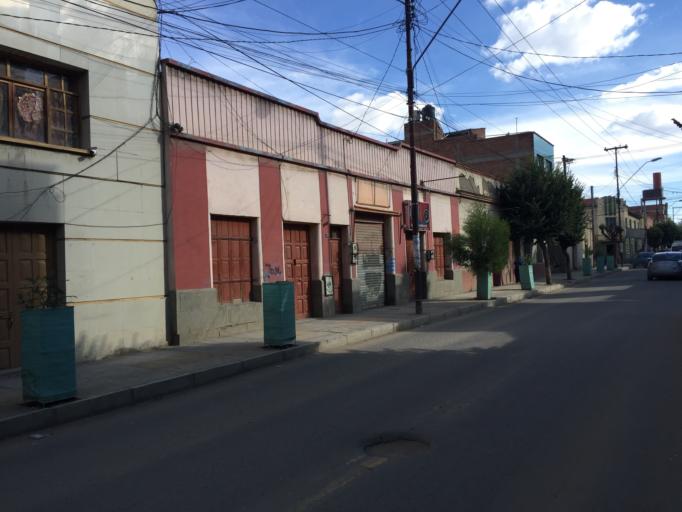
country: BO
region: Oruro
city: Oruro
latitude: -17.9769
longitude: -67.1112
